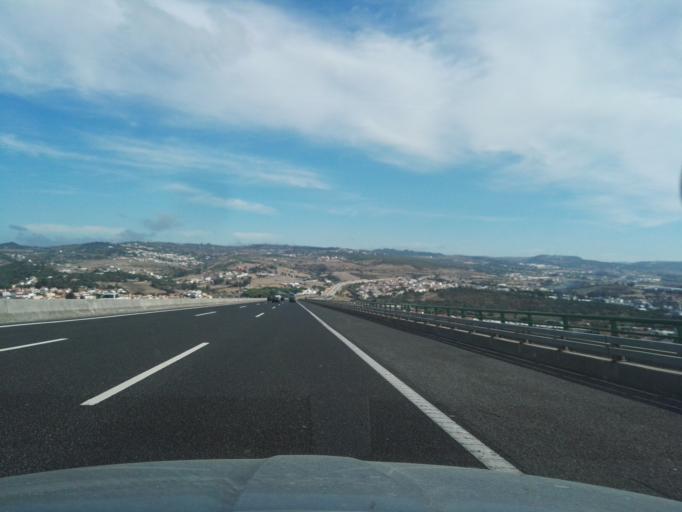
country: PT
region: Lisbon
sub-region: Loures
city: Loures
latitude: 38.8304
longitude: -9.1905
